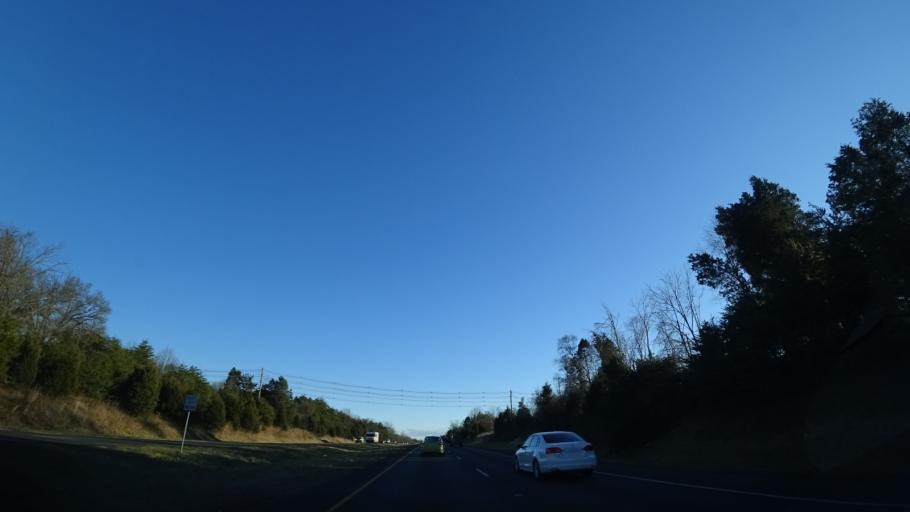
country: US
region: Virginia
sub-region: Prince William County
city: Bull Run
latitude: 38.7771
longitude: -77.5429
